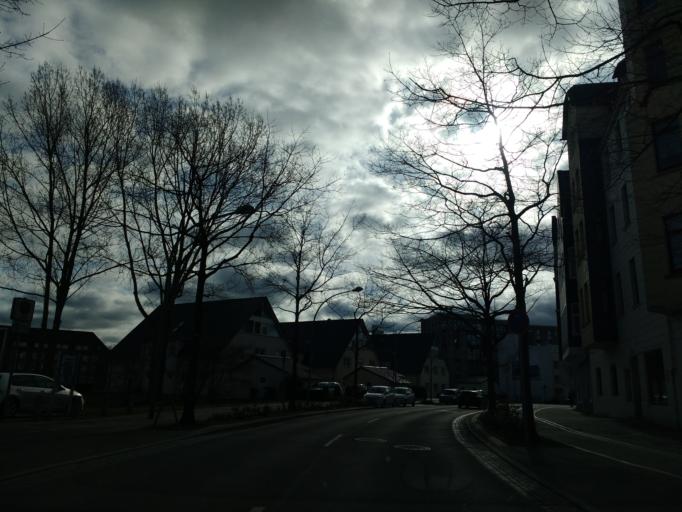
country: DE
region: Bremen
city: Bremerhaven
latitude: 53.5430
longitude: 8.5855
